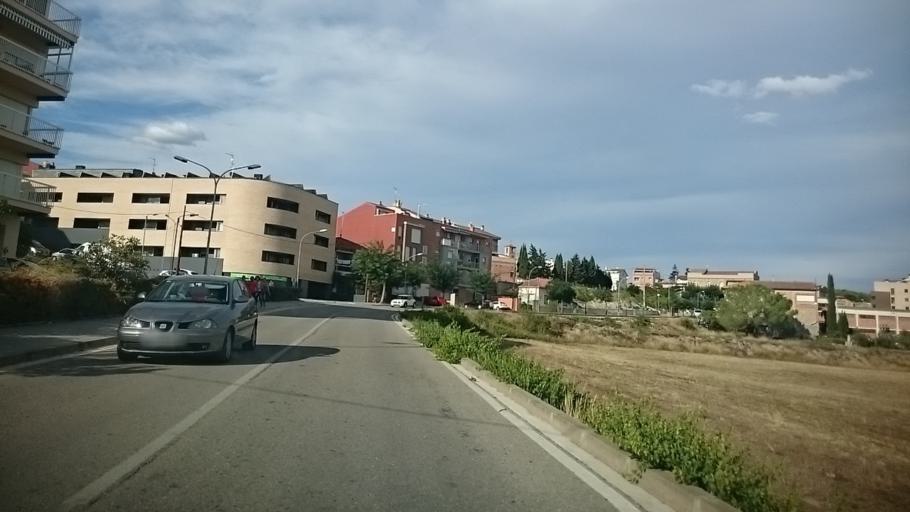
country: ES
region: Catalonia
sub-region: Provincia de Barcelona
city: Odena
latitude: 41.6037
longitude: 1.6402
